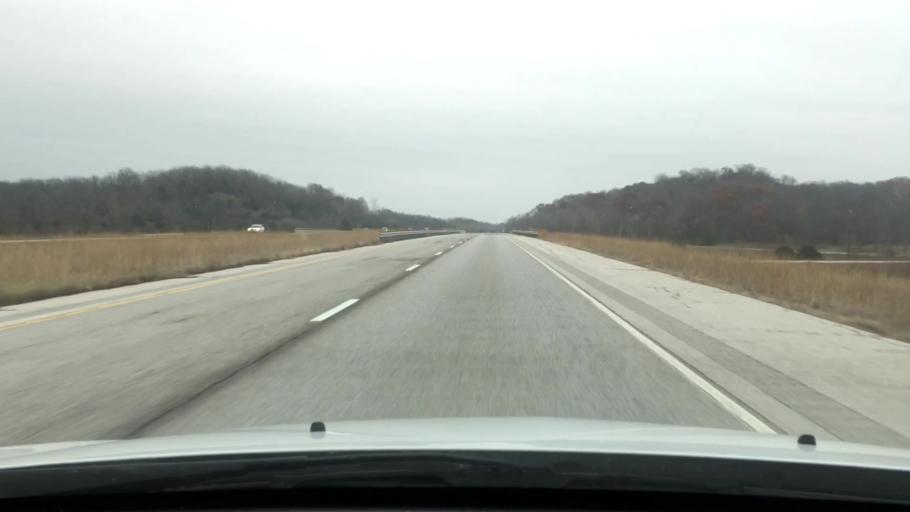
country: US
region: Illinois
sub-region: Scott County
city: Winchester
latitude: 39.6850
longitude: -90.5727
